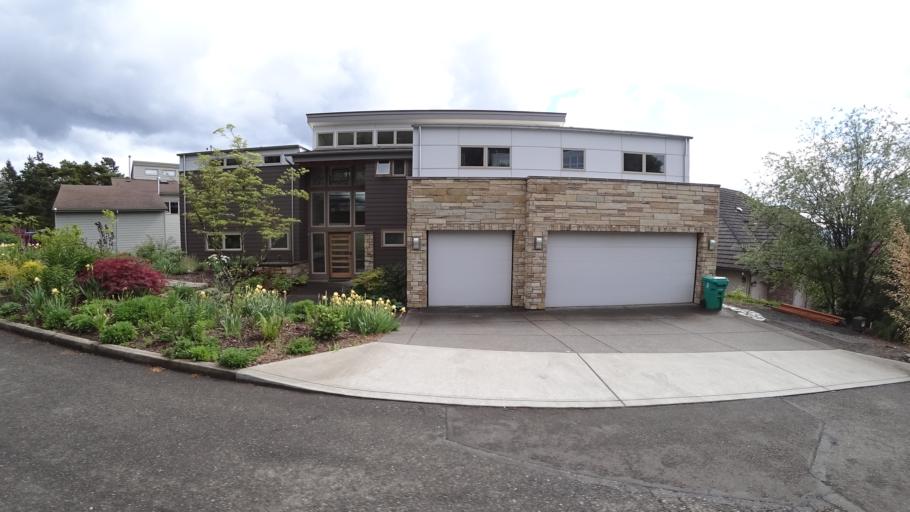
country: US
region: Oregon
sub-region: Washington County
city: West Haven
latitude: 45.5425
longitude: -122.7623
